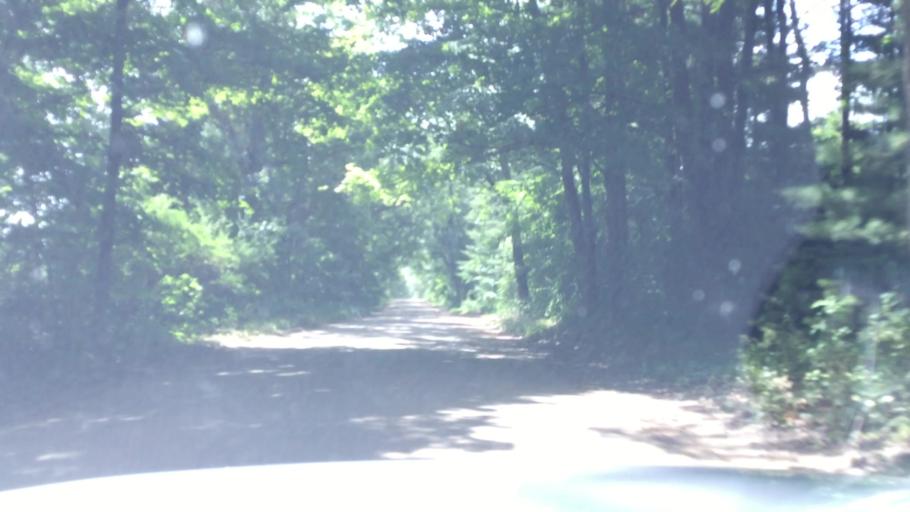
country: US
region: Michigan
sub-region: Ionia County
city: Belding
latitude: 43.1414
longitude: -85.2135
